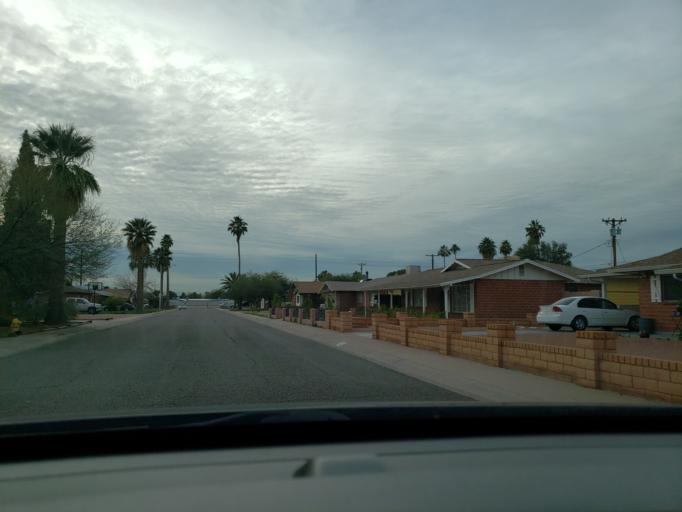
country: US
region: Arizona
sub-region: Maricopa County
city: Glendale
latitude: 33.5327
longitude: -112.1366
